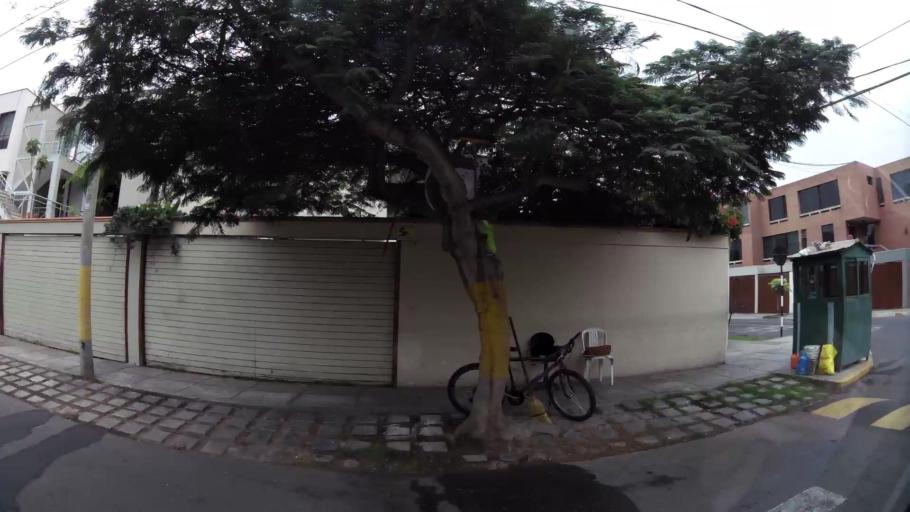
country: PE
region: Lima
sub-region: Lima
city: Surco
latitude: -12.1202
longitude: -77.0081
